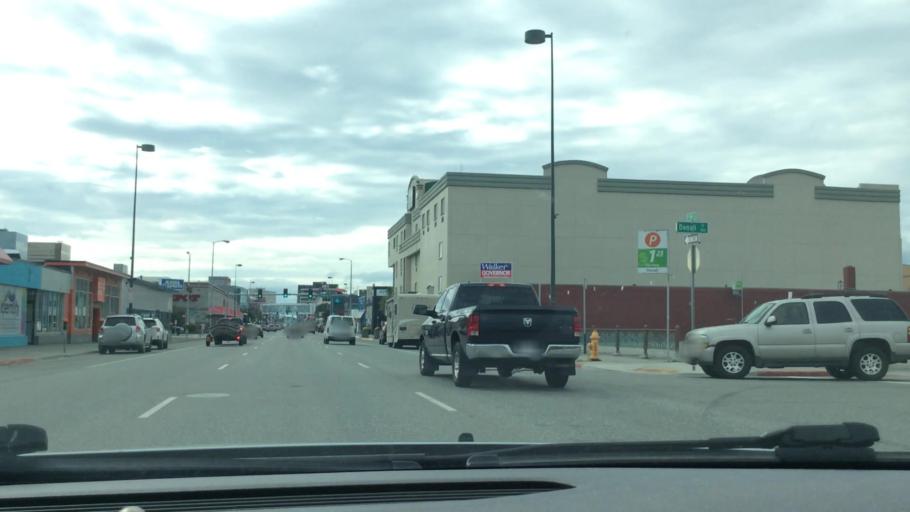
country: US
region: Alaska
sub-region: Anchorage Municipality
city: Anchorage
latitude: 61.2176
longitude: -149.8769
